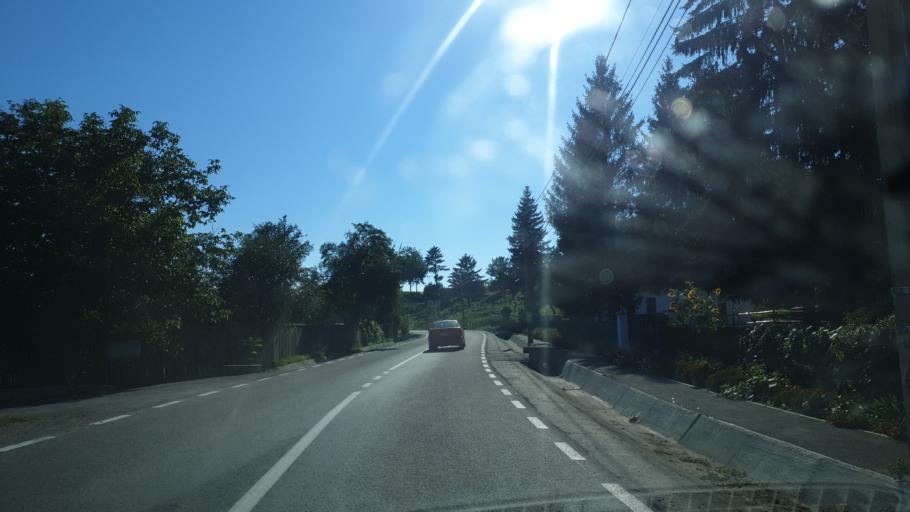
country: RO
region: Covasna
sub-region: Comuna Ilieni
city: Ilieni
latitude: 45.7917
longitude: 25.7670
